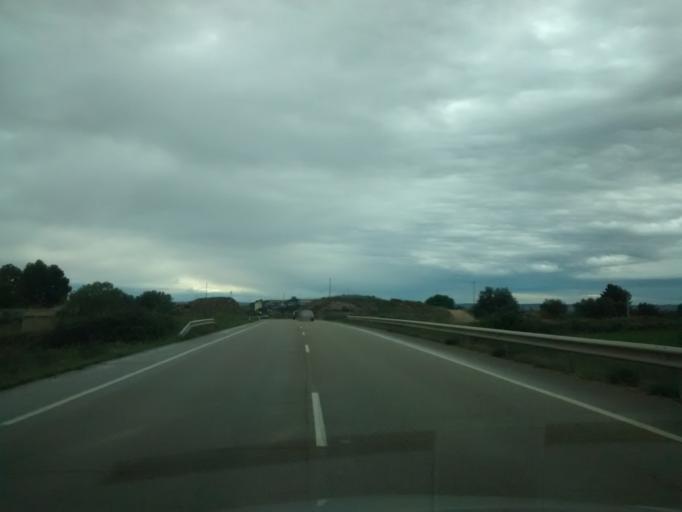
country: ES
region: Aragon
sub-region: Provincia de Zaragoza
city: Caspe
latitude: 41.2170
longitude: -0.0124
